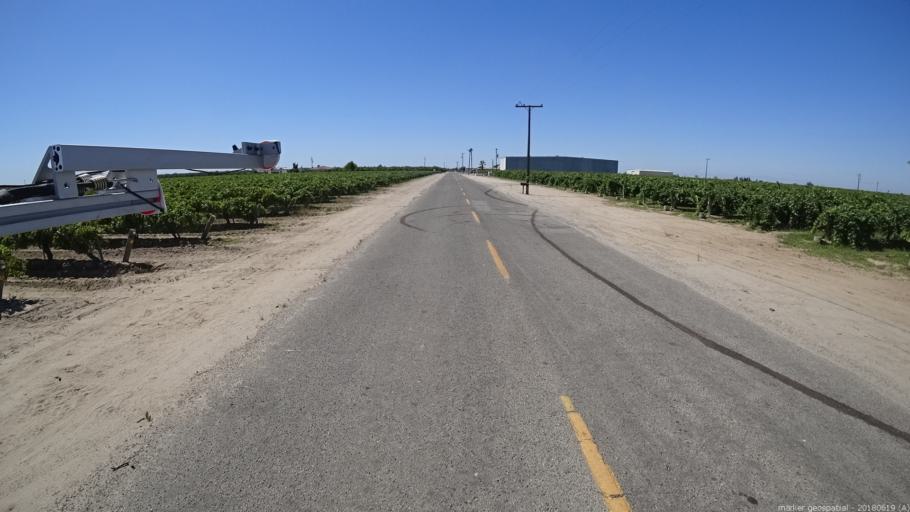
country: US
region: California
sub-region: Fresno County
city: Biola
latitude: 36.8434
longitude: -120.0649
